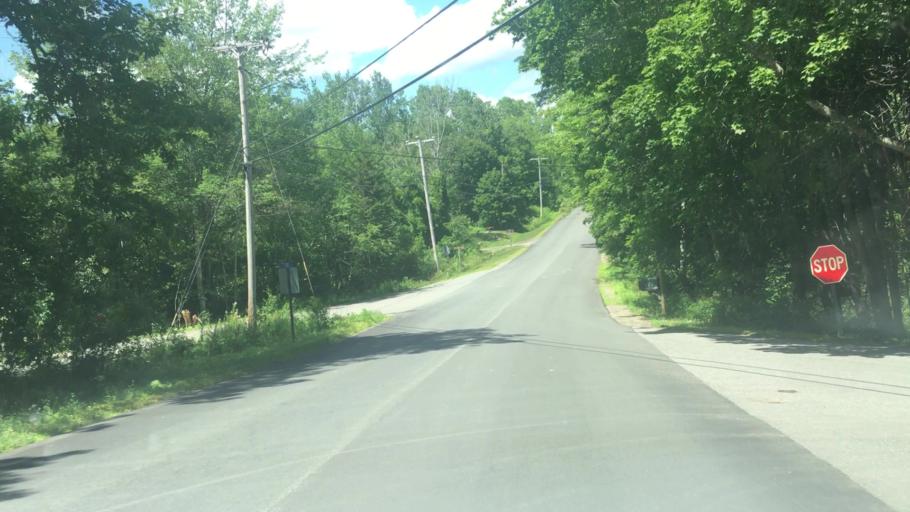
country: US
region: Maine
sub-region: Waldo County
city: Northport
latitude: 44.3814
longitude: -68.9735
